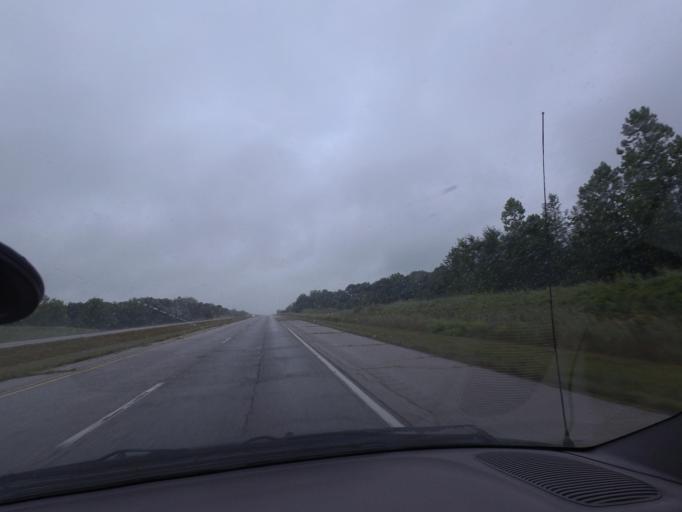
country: US
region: Illinois
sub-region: Pike County
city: Barry
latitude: 39.6918
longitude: -90.9383
